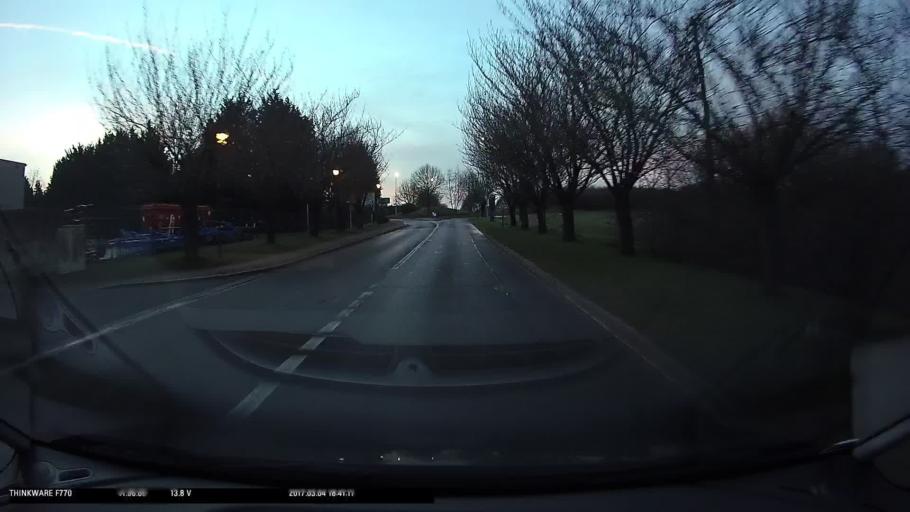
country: FR
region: Ile-de-France
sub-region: Departement du Val-d'Oise
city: Marines
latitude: 49.1483
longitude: 1.9711
